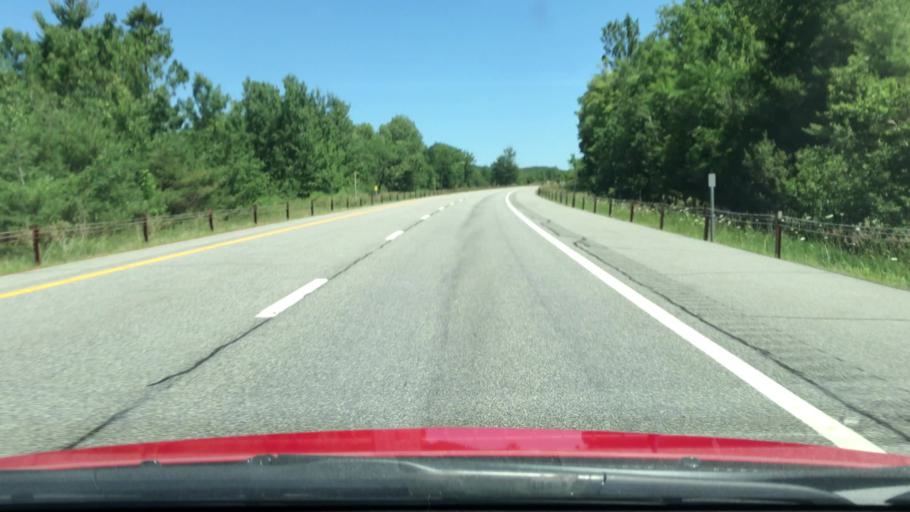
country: US
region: New York
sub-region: Essex County
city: Elizabethtown
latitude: 44.1765
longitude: -73.5799
